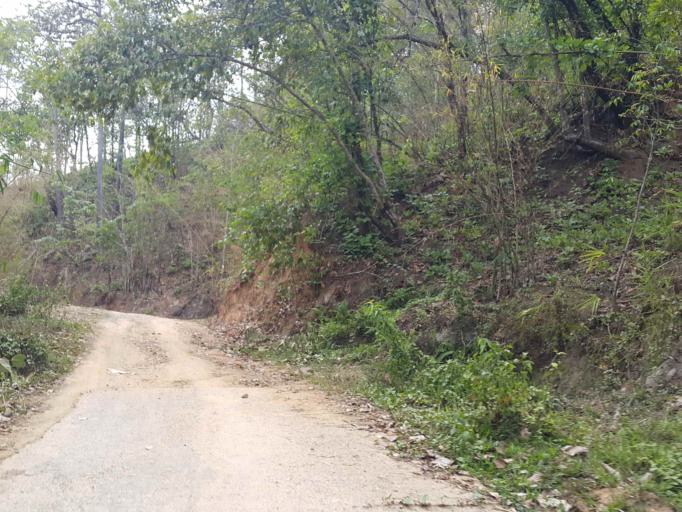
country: TH
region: Chiang Mai
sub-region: Amphoe Chiang Dao
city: Chiang Dao
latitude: 19.2940
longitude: 98.7553
